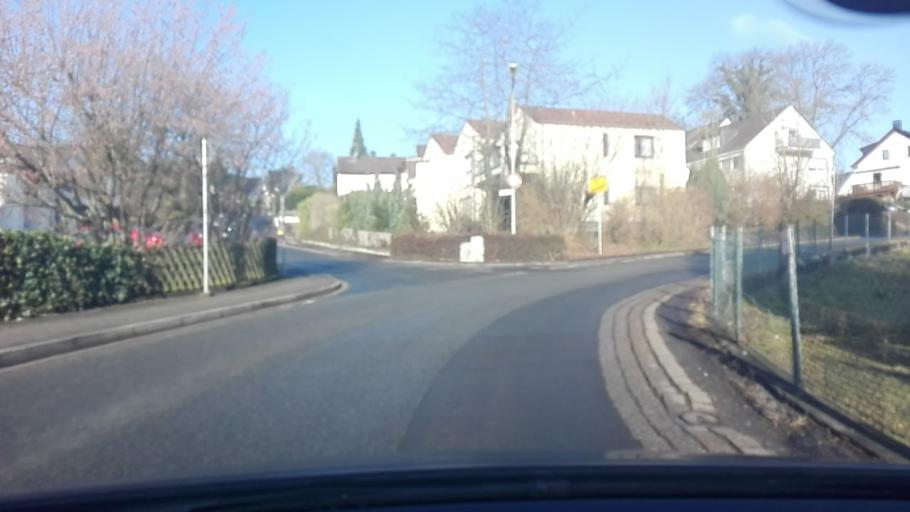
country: DE
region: North Rhine-Westphalia
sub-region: Regierungsbezirk Arnsberg
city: Frondenberg
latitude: 51.4775
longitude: 7.7681
